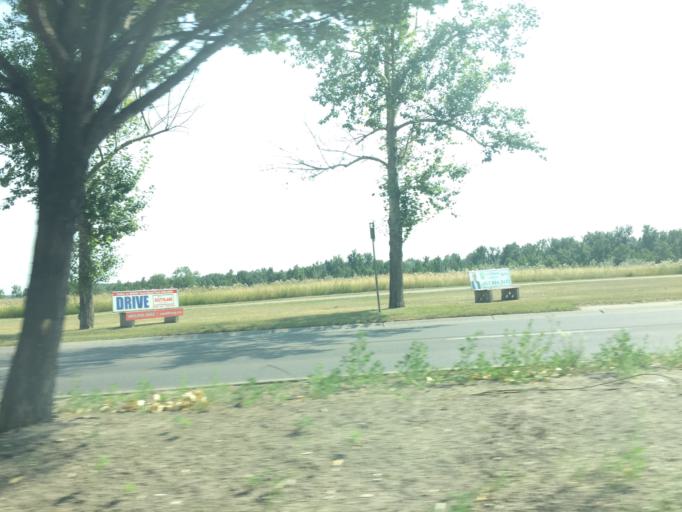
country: CA
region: Alberta
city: Calgary
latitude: 50.9305
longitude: -114.0580
